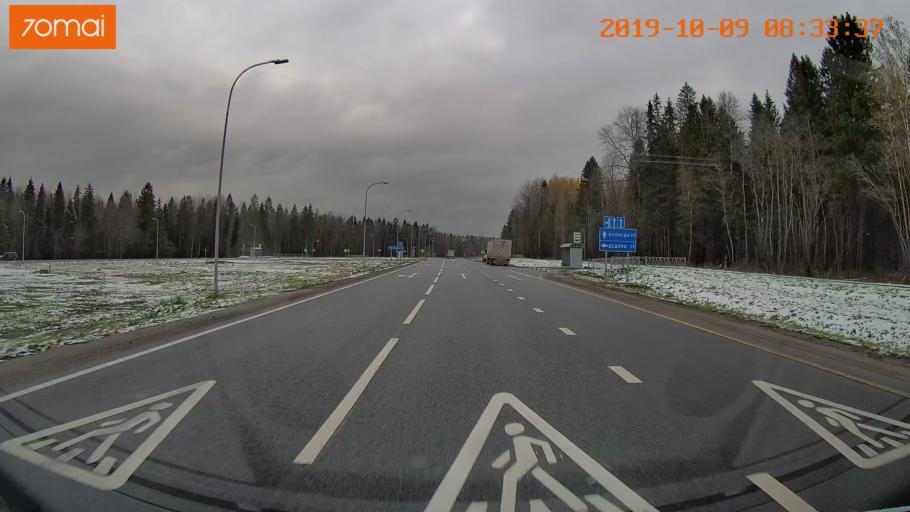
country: RU
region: Vologda
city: Gryazovets
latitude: 58.8848
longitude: 40.1918
